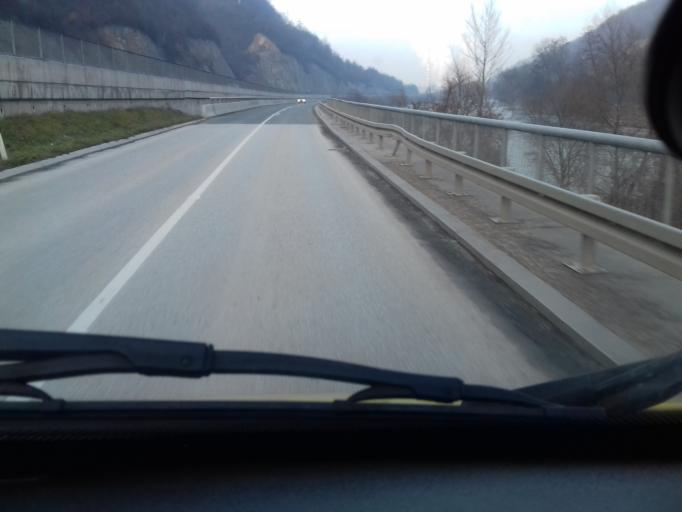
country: BA
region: Federation of Bosnia and Herzegovina
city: Dobrinje
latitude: 44.0603
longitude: 18.1035
